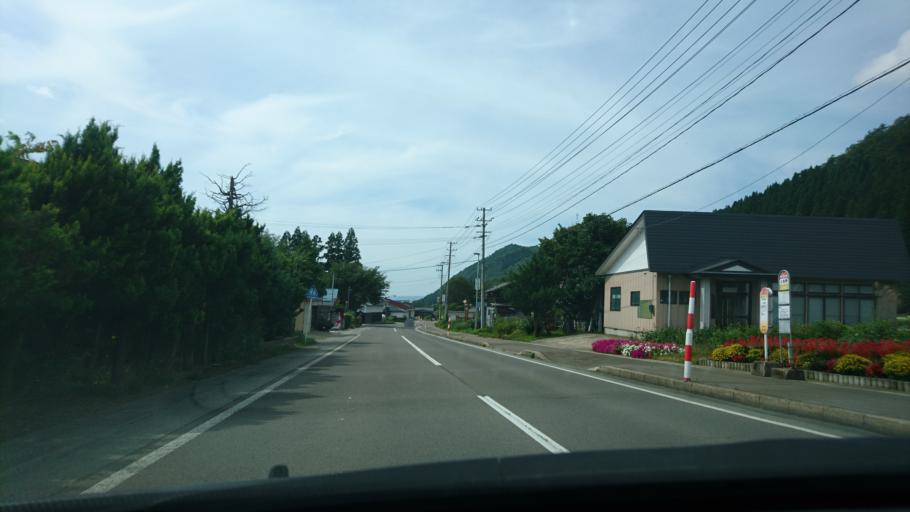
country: JP
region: Akita
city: Yuzawa
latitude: 39.1986
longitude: 140.6055
